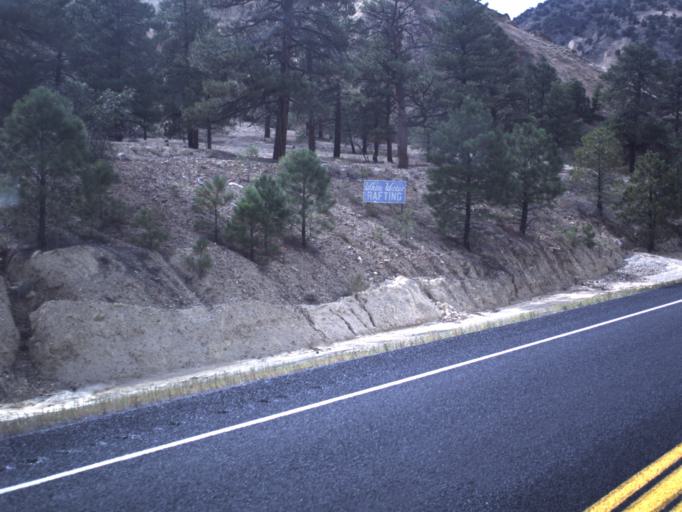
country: US
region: Utah
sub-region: Sevier County
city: Monroe
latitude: 38.5128
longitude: -112.2628
